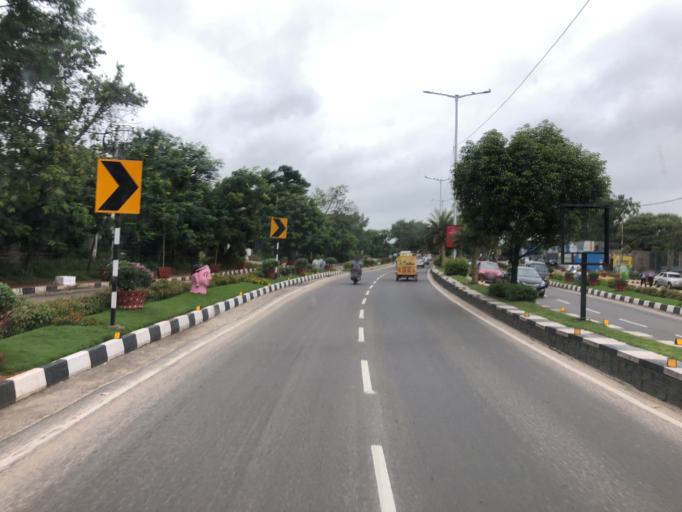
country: IN
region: Telangana
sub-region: Rangareddi
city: Kukatpalli
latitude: 17.4596
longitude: 78.3770
